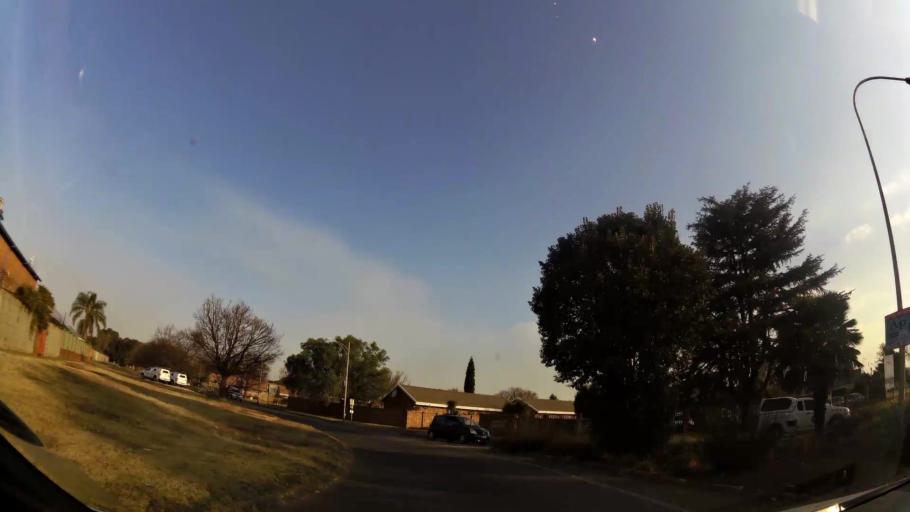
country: ZA
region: Gauteng
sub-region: Ekurhuleni Metropolitan Municipality
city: Springs
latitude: -26.2531
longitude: 28.4042
